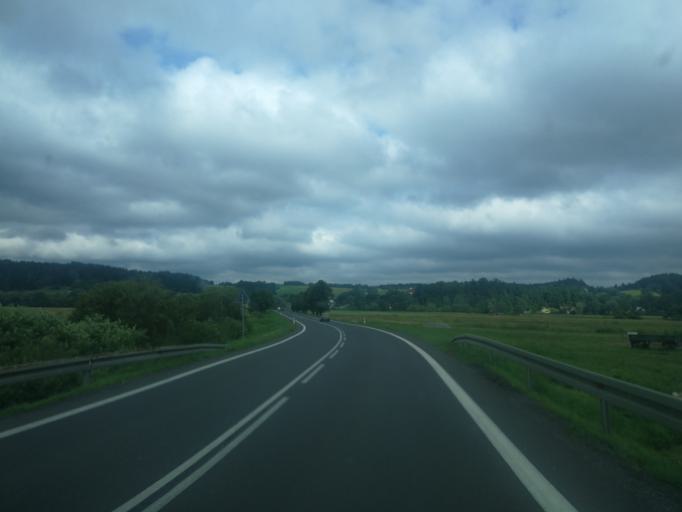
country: PL
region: Subcarpathian Voivodeship
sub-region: Powiat leski
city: Lesko
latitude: 49.4917
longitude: 22.3193
